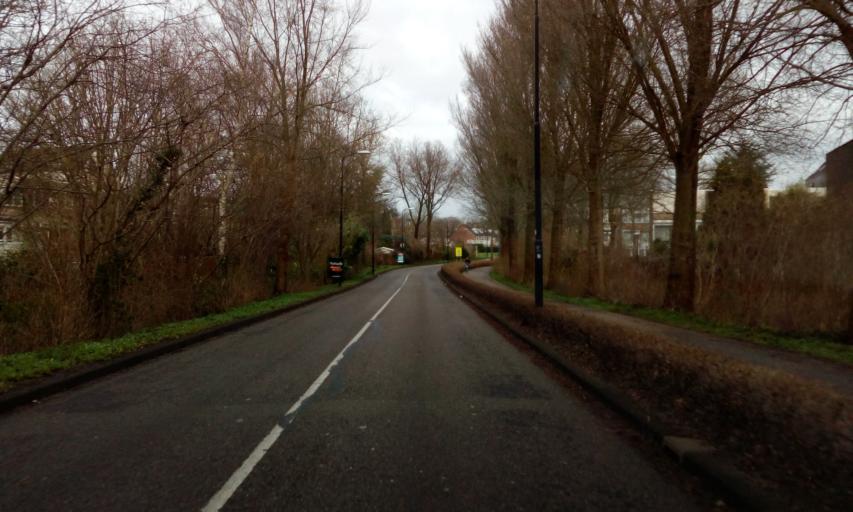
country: NL
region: Utrecht
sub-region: Gemeente De Ronde Venen
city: Mijdrecht
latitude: 52.2107
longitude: 4.8614
